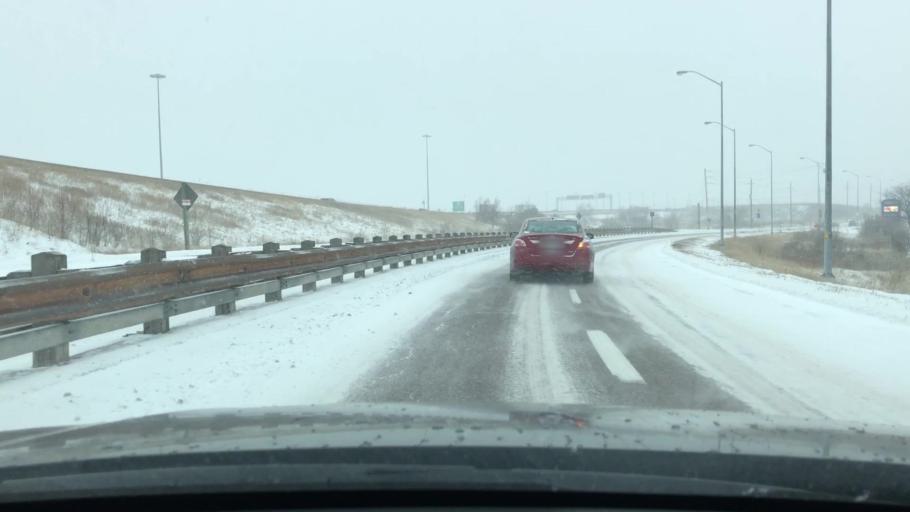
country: CA
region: Ontario
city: Etobicoke
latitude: 43.6725
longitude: -79.5885
